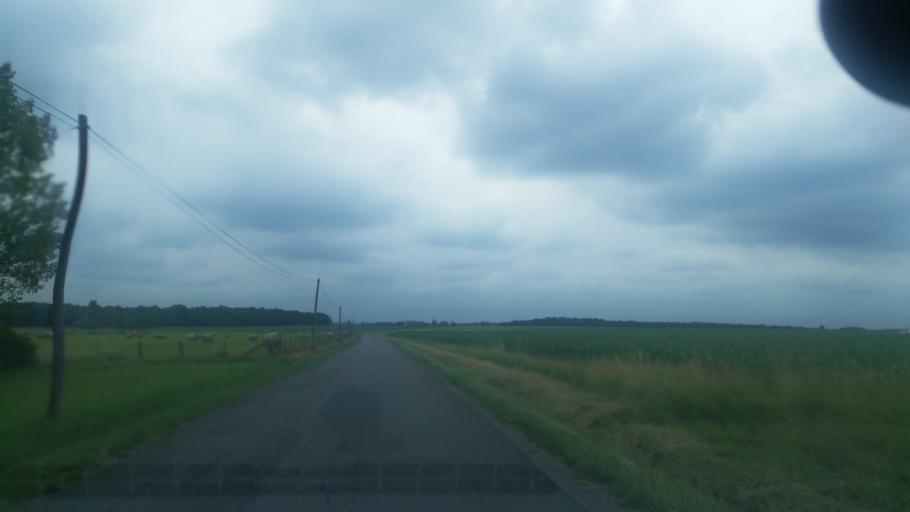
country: FR
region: Centre
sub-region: Departement du Loir-et-Cher
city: Saint-Romain-sur-Cher
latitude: 47.3473
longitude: 1.4426
